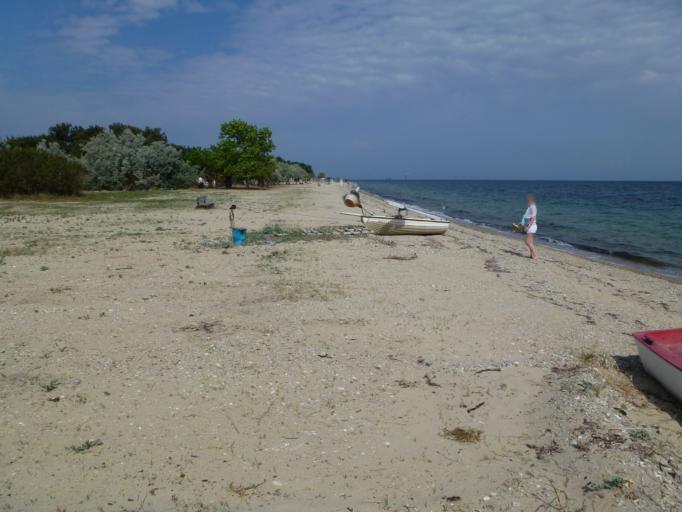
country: GR
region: East Macedonia and Thrace
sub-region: Nomos Kavalas
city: Prinos
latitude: 40.7600
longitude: 24.5715
